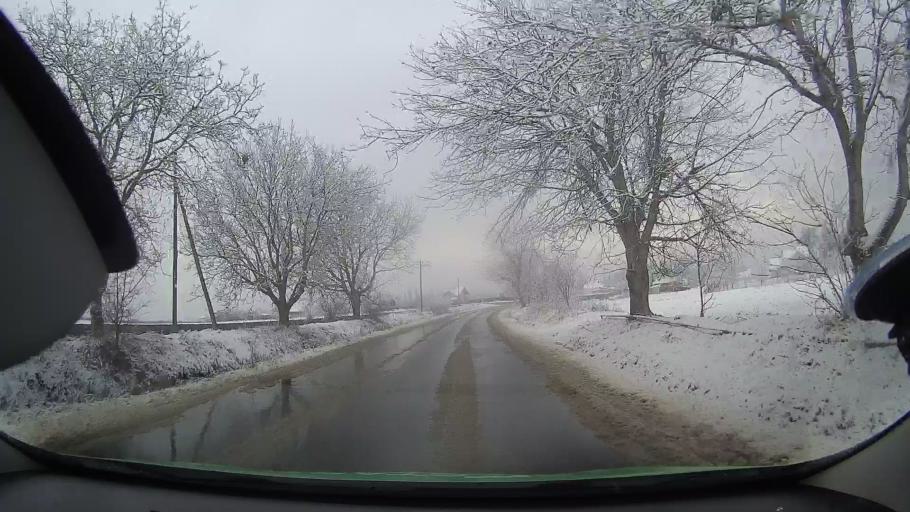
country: RO
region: Mures
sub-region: Comuna Bogata
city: Bogata
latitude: 46.4527
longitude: 24.0834
